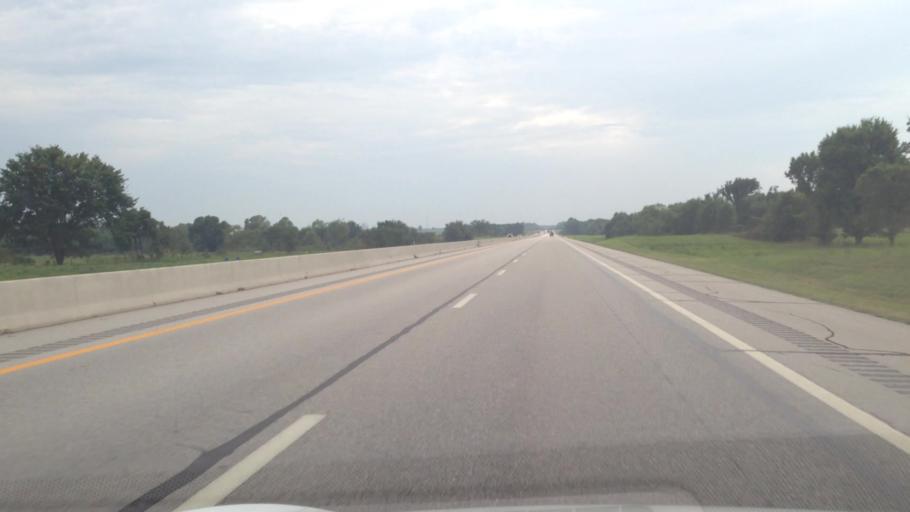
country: US
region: Kansas
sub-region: Cherokee County
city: Baxter Springs
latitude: 36.9653
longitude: -94.6569
